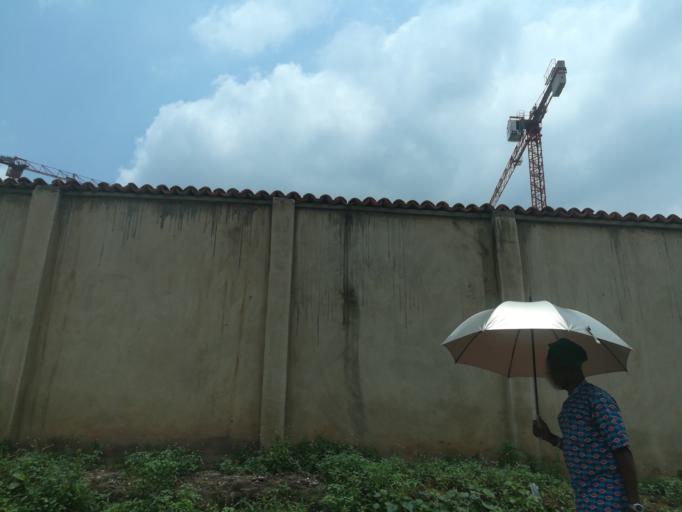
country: NG
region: Lagos
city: Ojota
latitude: 6.5948
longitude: 3.3688
